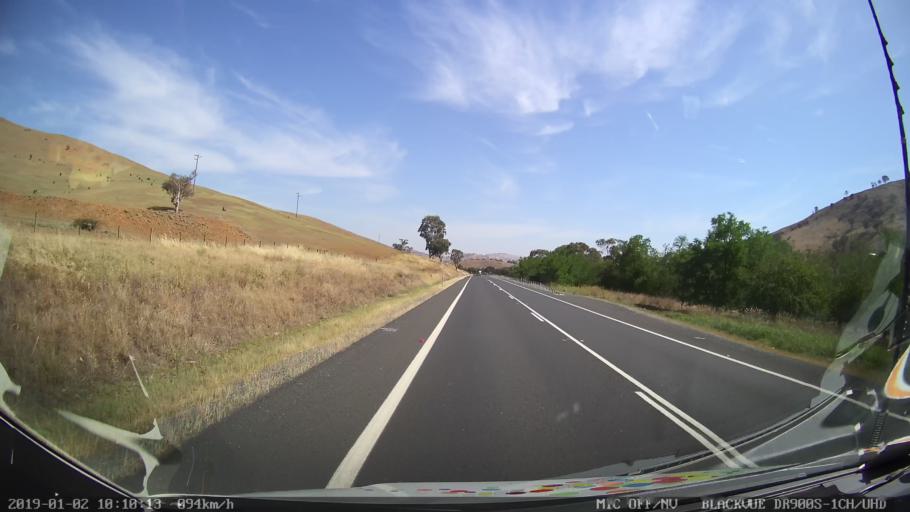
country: AU
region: New South Wales
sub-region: Gundagai
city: Gundagai
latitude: -35.1070
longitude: 148.0968
